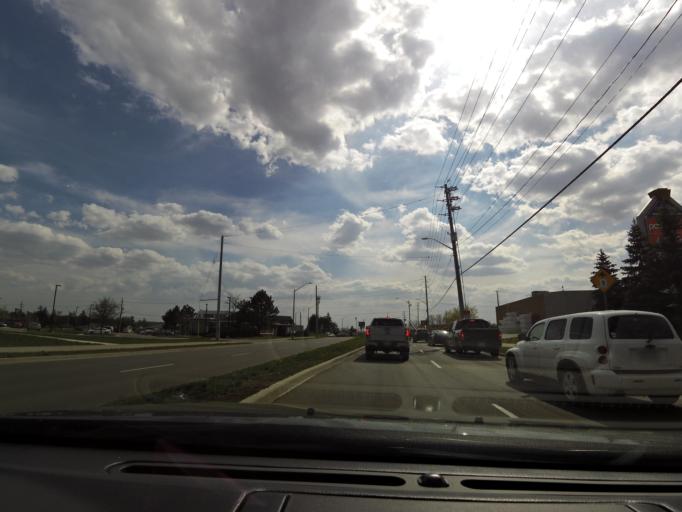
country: CA
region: Ontario
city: Cambridge
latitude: 43.3558
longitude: -80.2864
